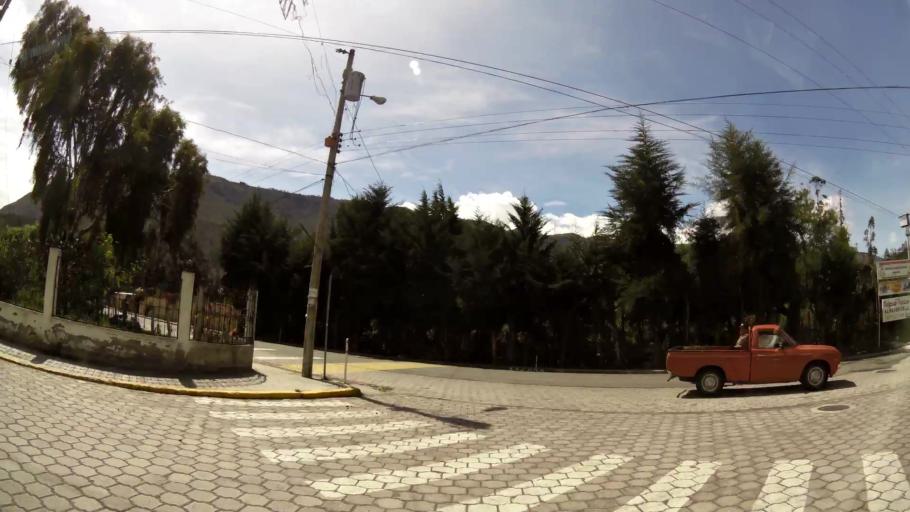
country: EC
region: Chimborazo
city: Guano
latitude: -1.5618
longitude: -78.5306
